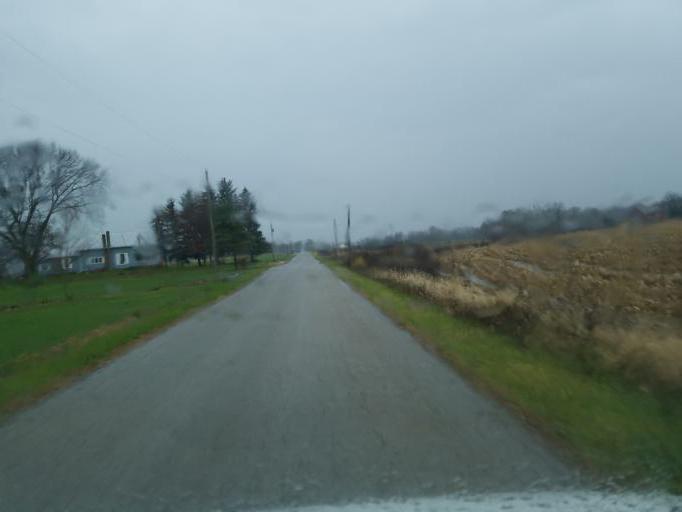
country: US
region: Ohio
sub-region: Morrow County
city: Cardington
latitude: 40.4527
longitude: -82.8716
